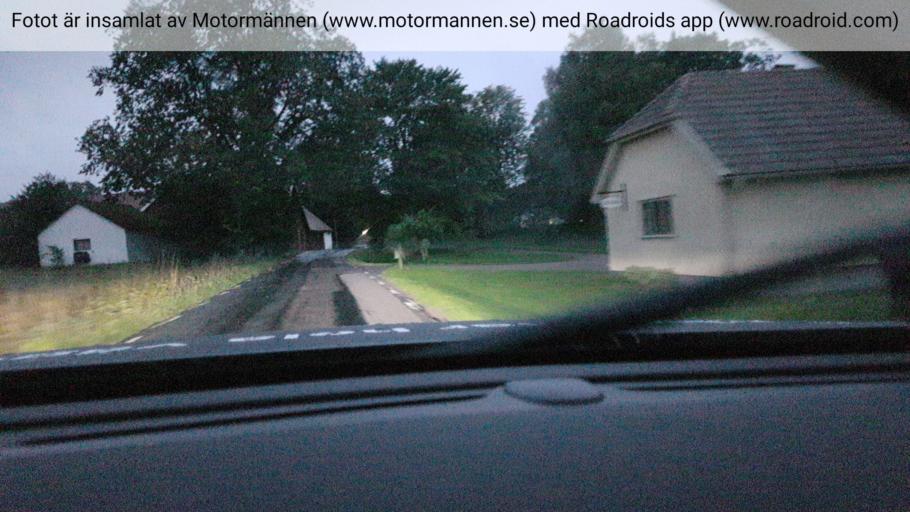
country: SE
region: Vaestra Goetaland
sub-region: Tidaholms Kommun
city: Tidaholm
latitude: 58.1707
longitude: 13.8224
